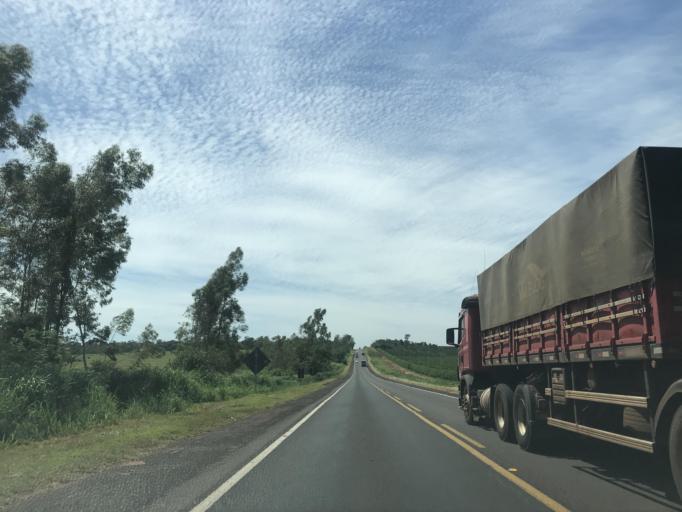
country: BR
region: Parana
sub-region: Paranavai
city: Nova Aurora
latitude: -22.9588
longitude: -52.6523
